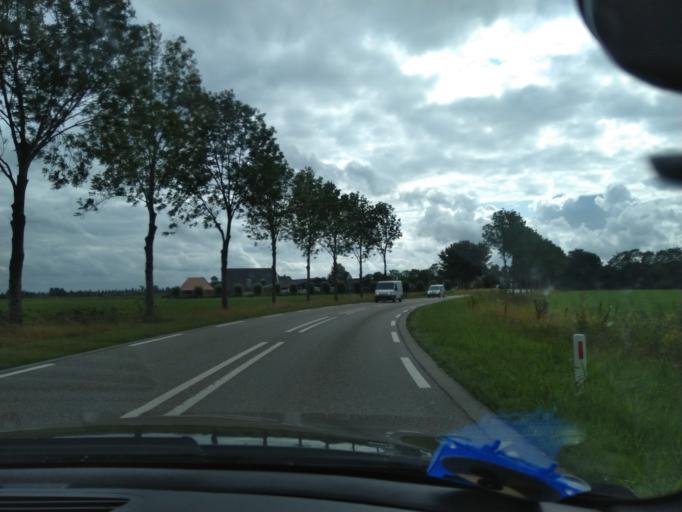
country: NL
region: Groningen
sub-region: Gemeente Zuidhorn
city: Grijpskerk
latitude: 53.2633
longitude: 6.3191
